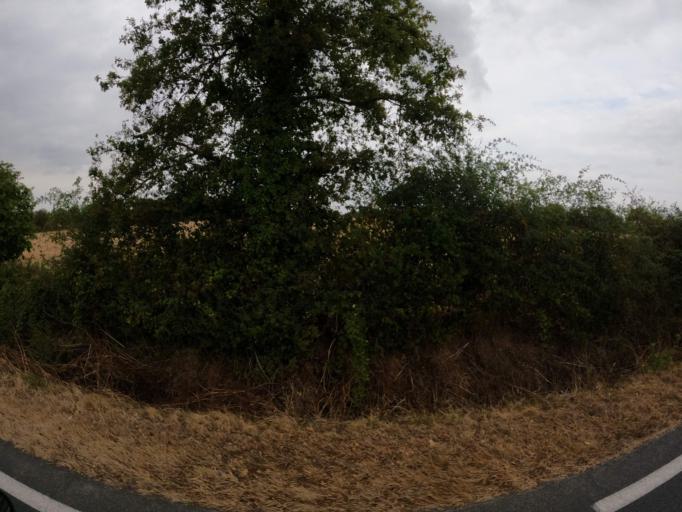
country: FR
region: Pays de la Loire
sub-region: Departement de la Vendee
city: Les Landes-Genusson
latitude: 46.9873
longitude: -1.1440
